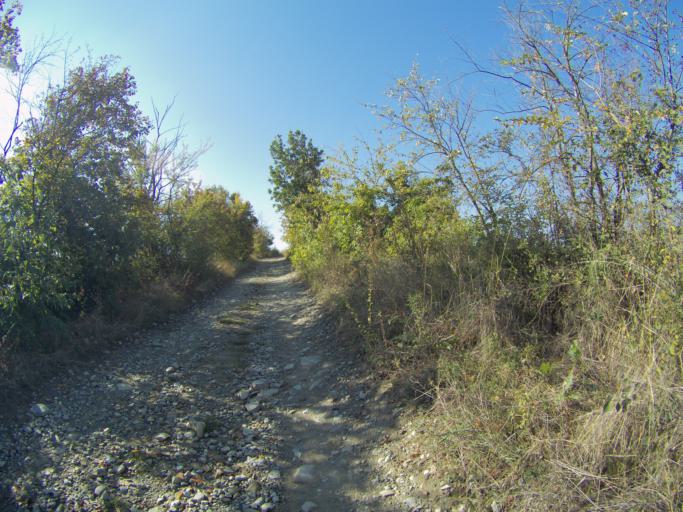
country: IT
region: Emilia-Romagna
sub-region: Provincia di Reggio Emilia
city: Vezzano sul Crostolo
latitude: 44.6147
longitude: 10.5482
